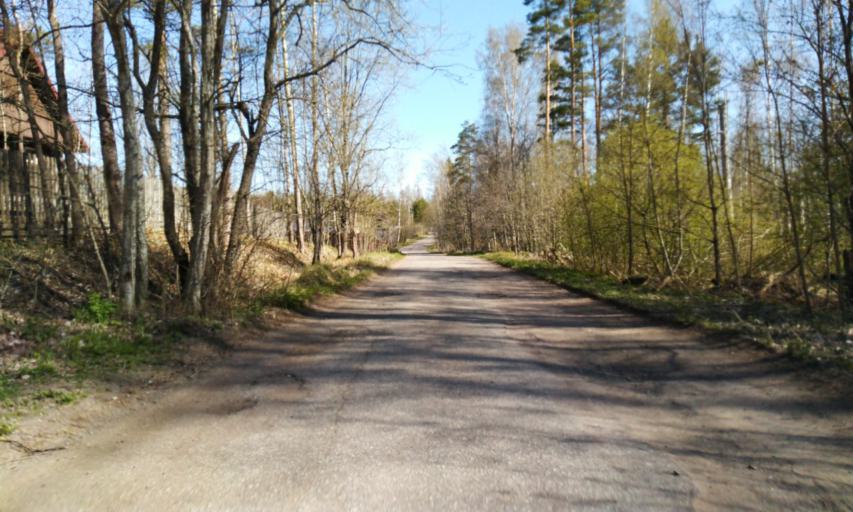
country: RU
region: Leningrad
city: Garbolovo
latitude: 60.3912
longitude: 30.4882
